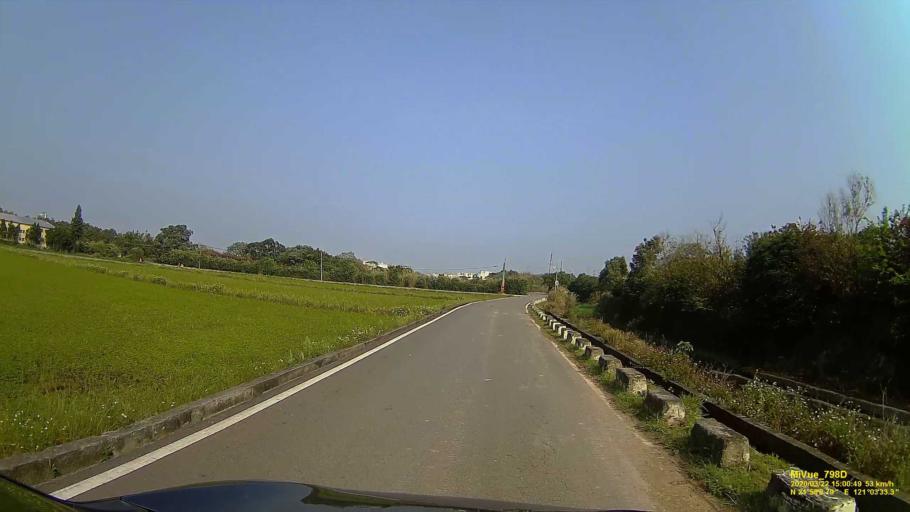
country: TW
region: Taiwan
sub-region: Hsinchu
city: Zhubei
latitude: 24.9690
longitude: 121.0597
